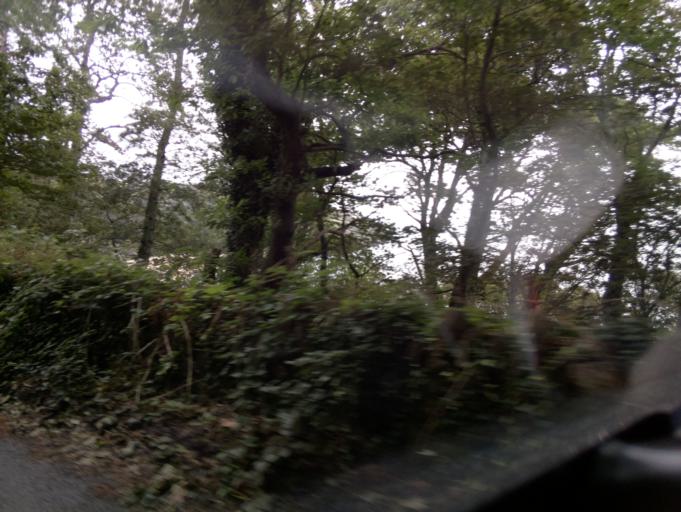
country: GB
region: England
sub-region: Devon
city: Dartmouth
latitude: 50.3169
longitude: -3.6138
